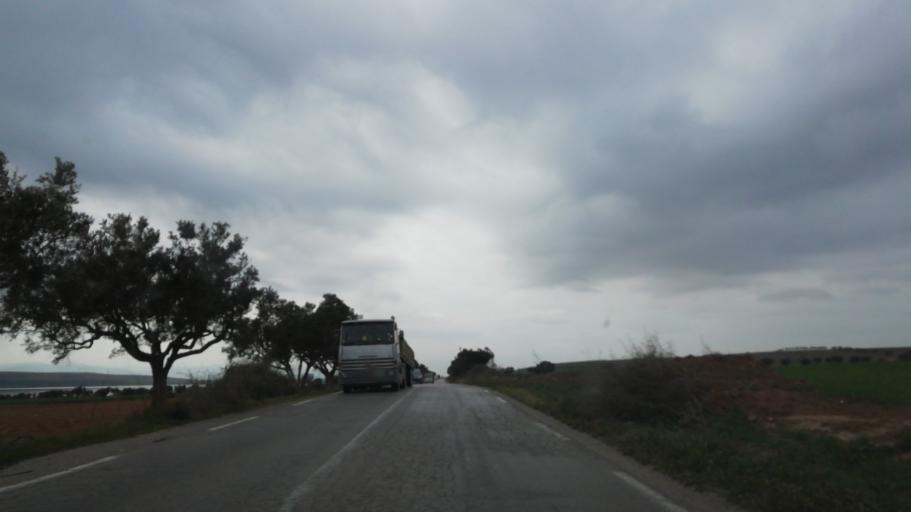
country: DZ
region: Oran
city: Sidi ech Chahmi
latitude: 35.6165
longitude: -0.4183
